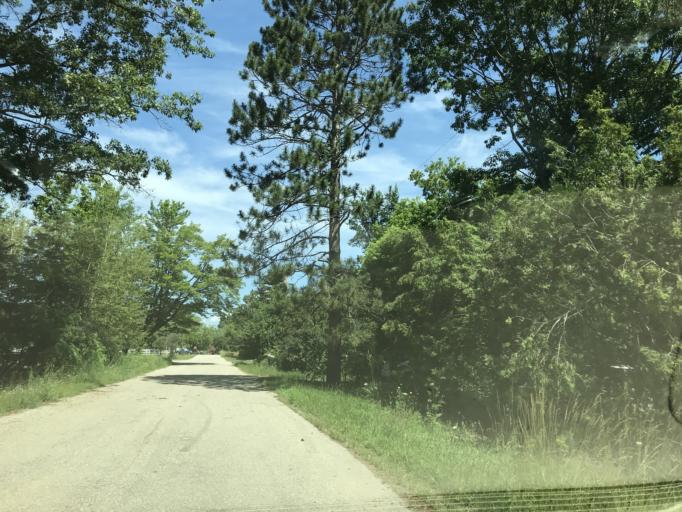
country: US
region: Michigan
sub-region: Roscommon County
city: Houghton Lake
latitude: 44.3294
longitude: -84.9431
